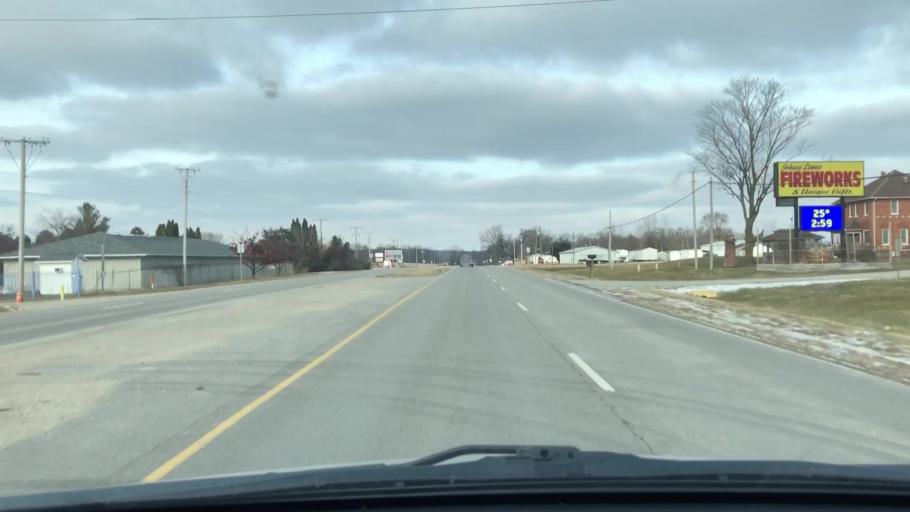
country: US
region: Indiana
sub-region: Steuben County
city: Angola
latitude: 41.6751
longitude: -85.0287
